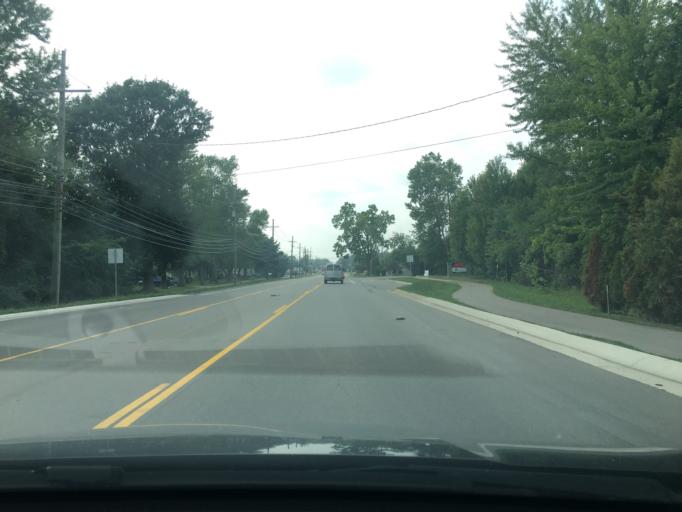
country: US
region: Michigan
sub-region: Oakland County
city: Rochester Hills
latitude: 42.6353
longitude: -83.1646
